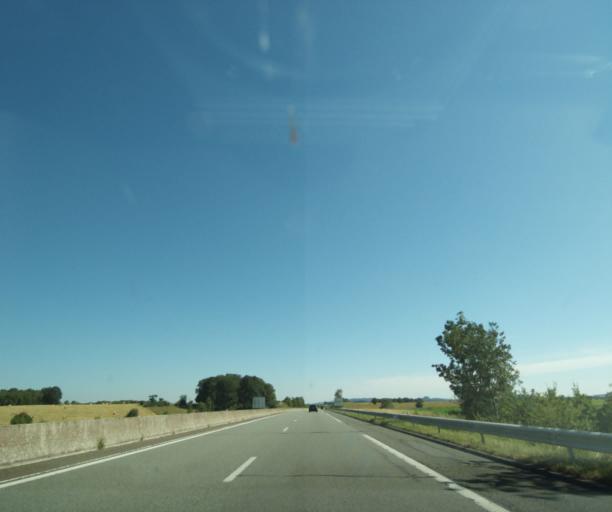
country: FR
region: Champagne-Ardenne
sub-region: Departement de la Haute-Marne
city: Avrecourt
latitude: 48.0038
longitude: 5.5166
